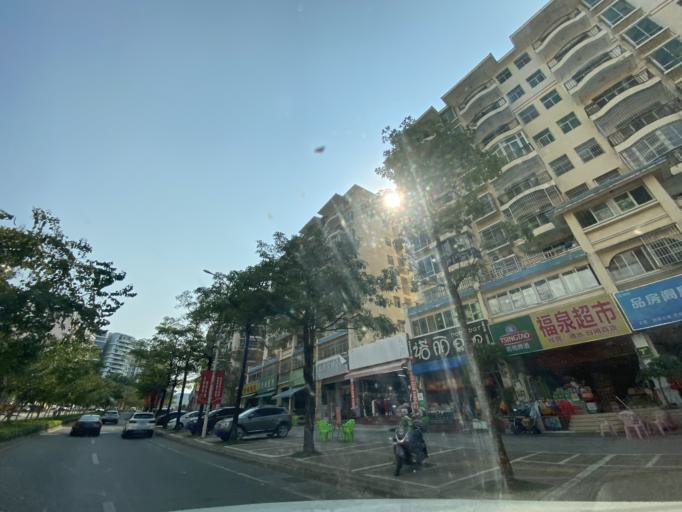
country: CN
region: Hainan
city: Chongshan
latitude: 18.7698
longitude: 109.5260
